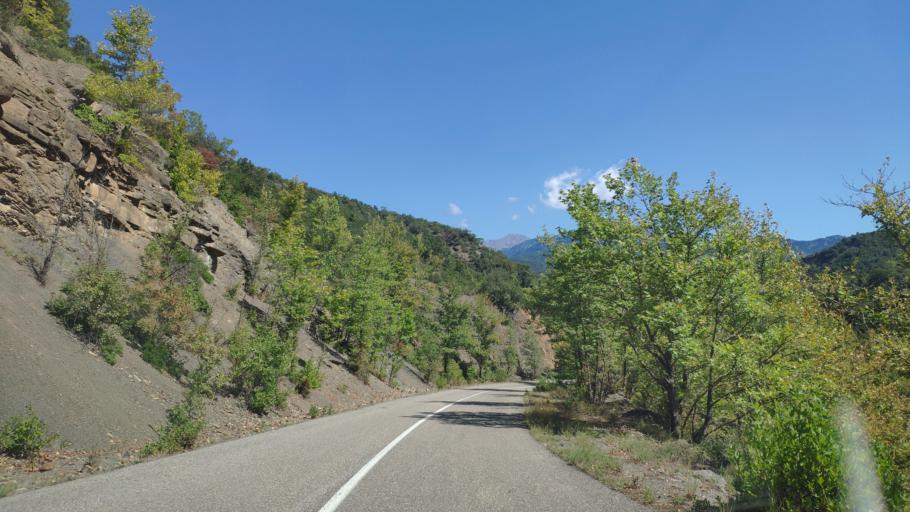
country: GR
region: Central Greece
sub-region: Nomos Evrytanias
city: Kerasochori
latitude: 38.9975
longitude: 21.5139
